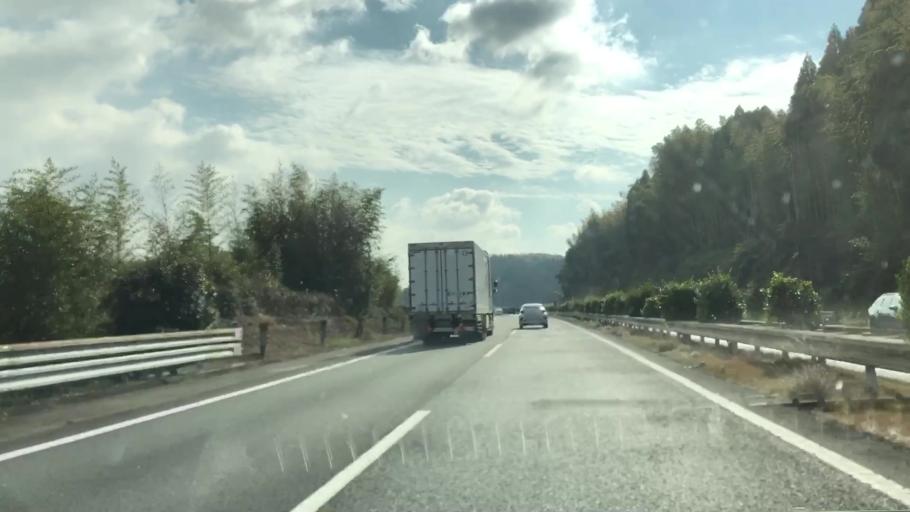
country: JP
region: Fukuoka
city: Setakamachi-takayanagi
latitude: 33.0821
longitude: 130.5416
